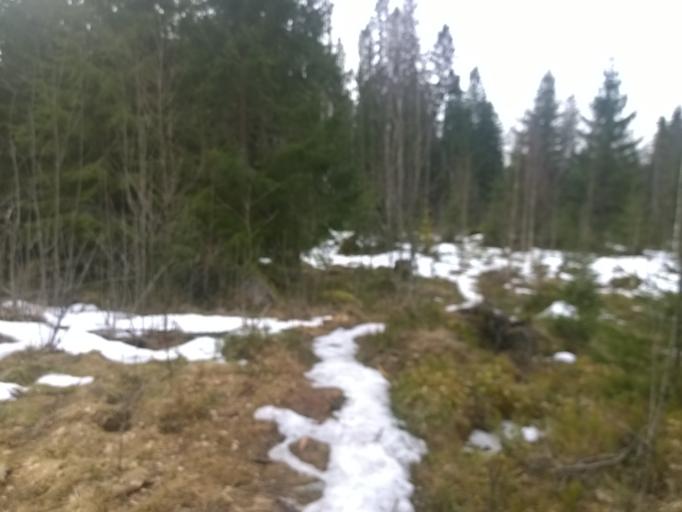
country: FI
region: Pirkanmaa
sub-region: Tampere
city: Tampere
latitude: 61.4480
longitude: 23.8231
